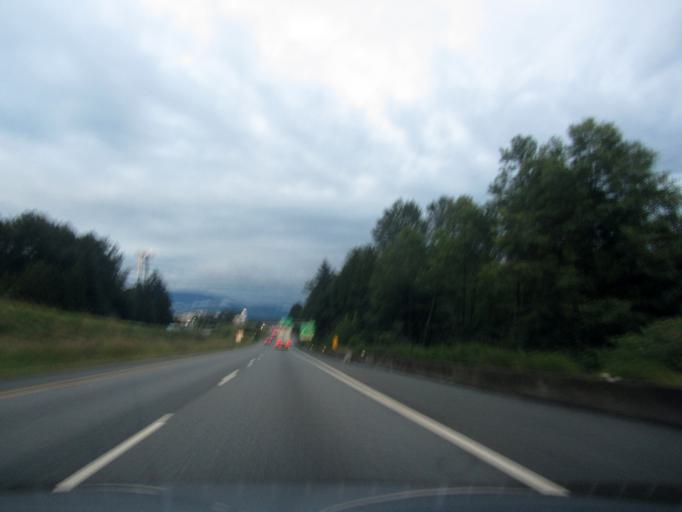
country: CA
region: British Columbia
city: Aldergrove
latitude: 49.0631
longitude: -122.3959
